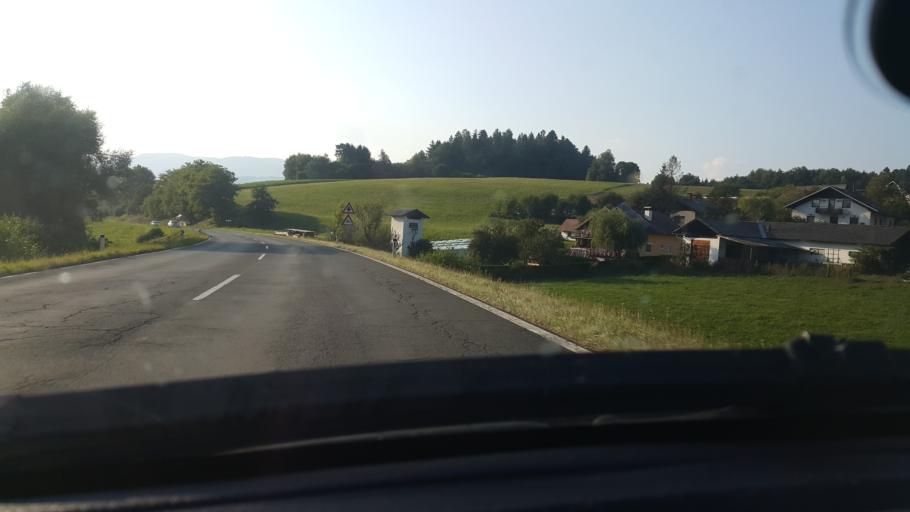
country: AT
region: Carinthia
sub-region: Politischer Bezirk Feldkirchen
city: Feldkirchen in Karnten
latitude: 46.7083
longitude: 14.1178
